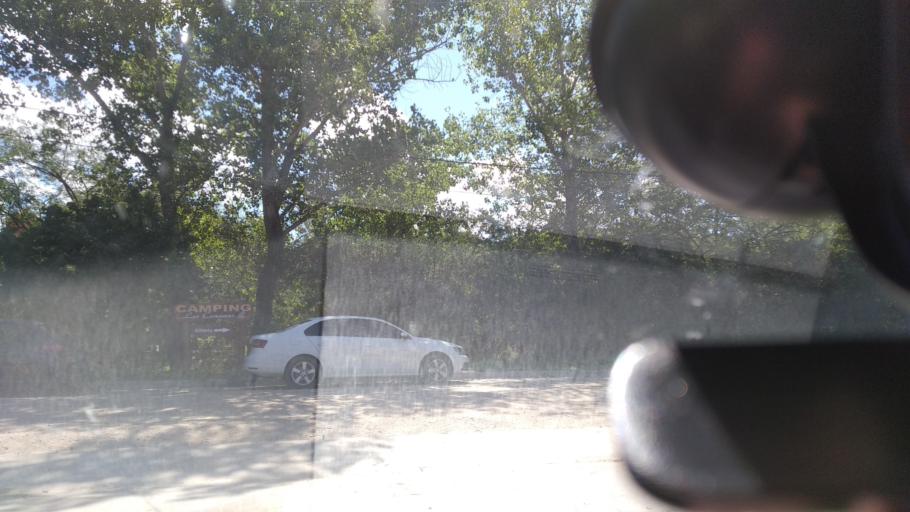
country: AR
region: Cordoba
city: Mina Clavero
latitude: -31.7242
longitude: -65.0121
